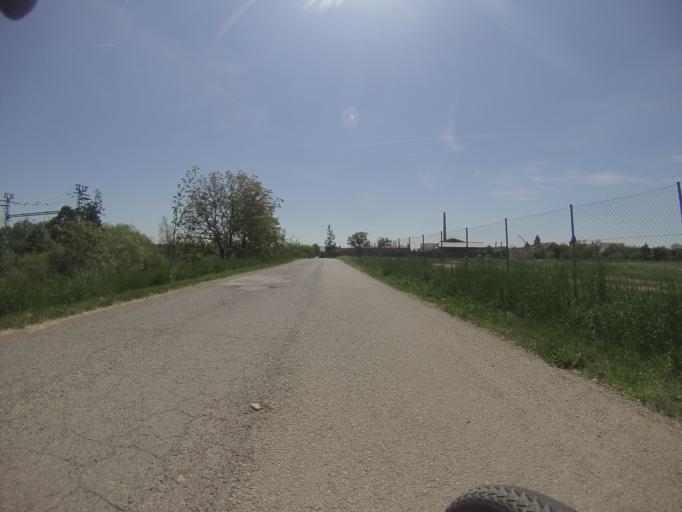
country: CZ
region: South Moravian
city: Vranovice
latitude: 48.9697
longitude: 16.6012
